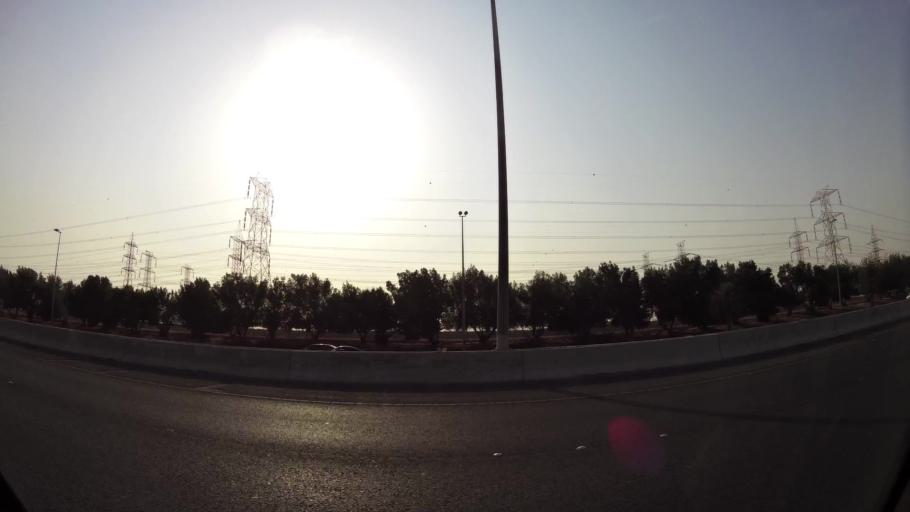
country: KW
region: Mubarak al Kabir
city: Sabah as Salim
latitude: 29.2574
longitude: 48.0449
